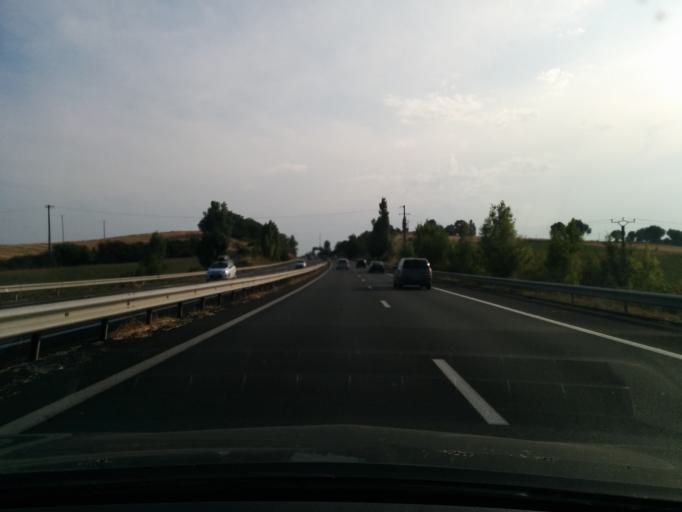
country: FR
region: Midi-Pyrenees
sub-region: Departement de la Haute-Garonne
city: Montastruc-la-Conseillere
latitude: 43.7362
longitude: 1.5832
